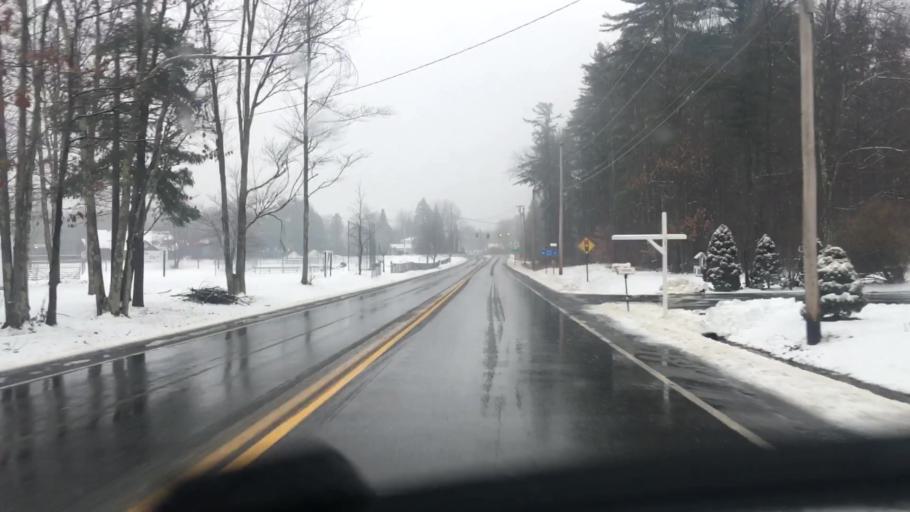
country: US
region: Maine
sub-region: York County
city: Buxton
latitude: 43.6023
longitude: -70.5357
